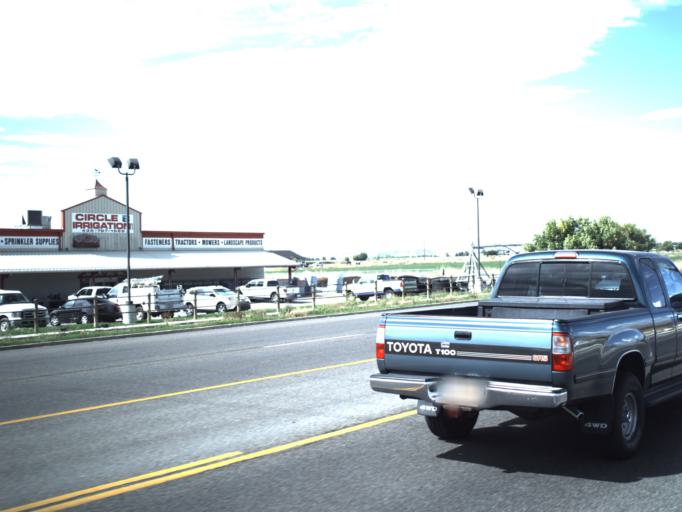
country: US
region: Utah
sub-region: Cache County
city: Hyde Park
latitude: 41.8059
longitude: -111.8333
